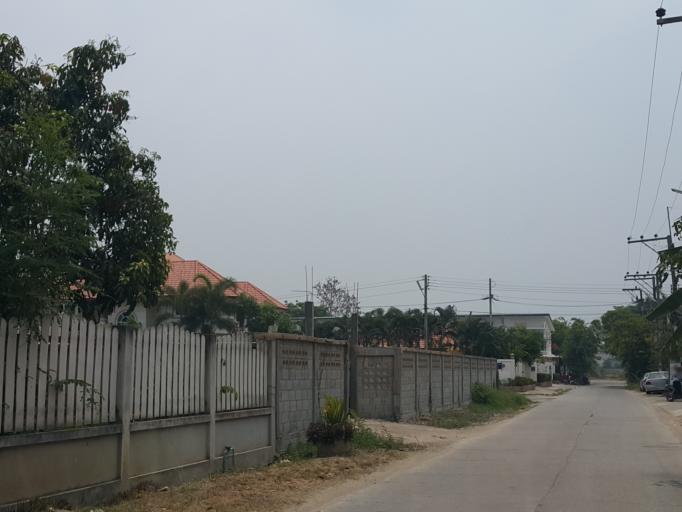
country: TH
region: Chiang Mai
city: Saraphi
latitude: 18.7516
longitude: 99.0366
